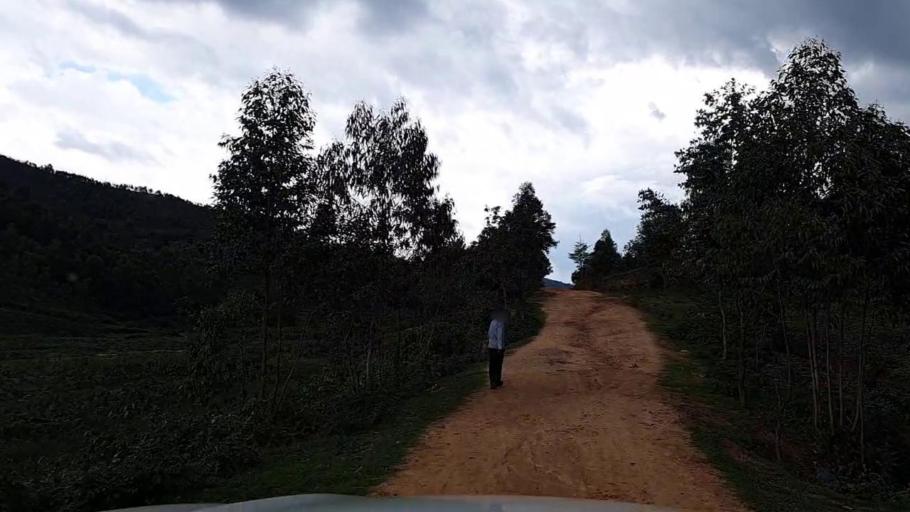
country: RW
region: Southern Province
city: Nyanza
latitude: -2.3927
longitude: 29.6923
